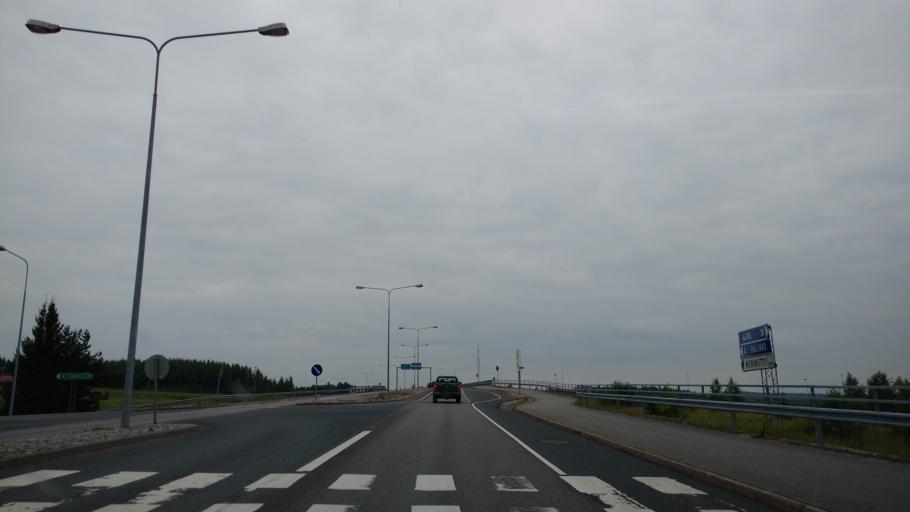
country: FI
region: Varsinais-Suomi
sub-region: Salo
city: Halikko
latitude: 60.4284
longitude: 23.0473
